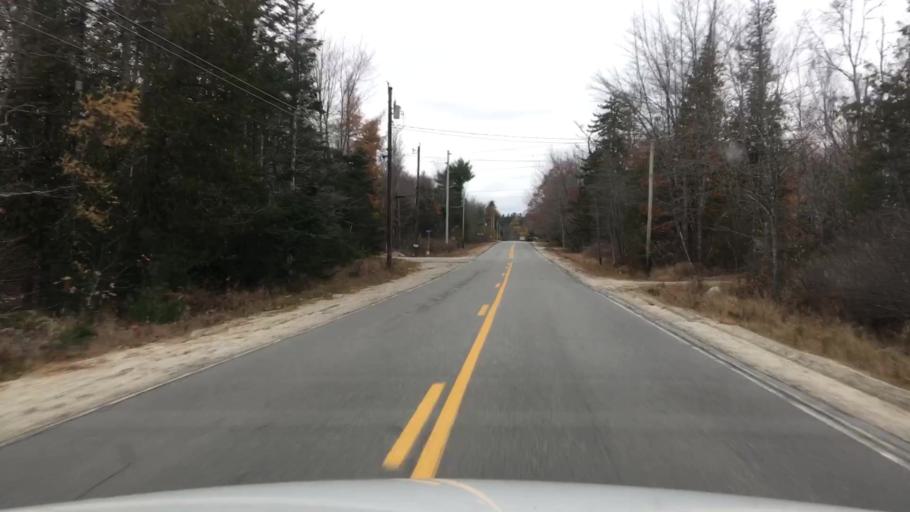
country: US
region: Maine
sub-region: Hancock County
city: Penobscot
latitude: 44.4194
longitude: -68.6161
